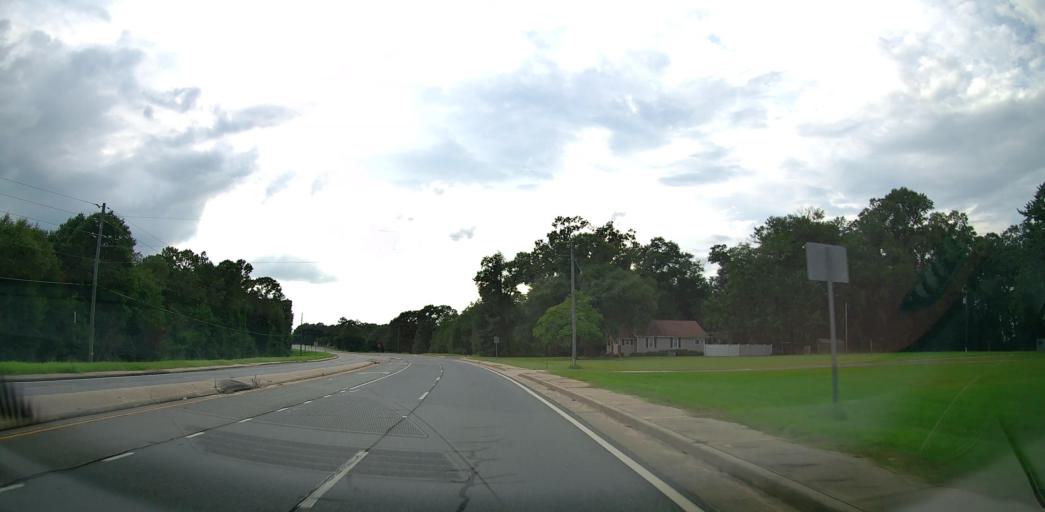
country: US
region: Georgia
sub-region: Pulaski County
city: Hawkinsville
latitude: 32.2808
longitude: -83.4323
